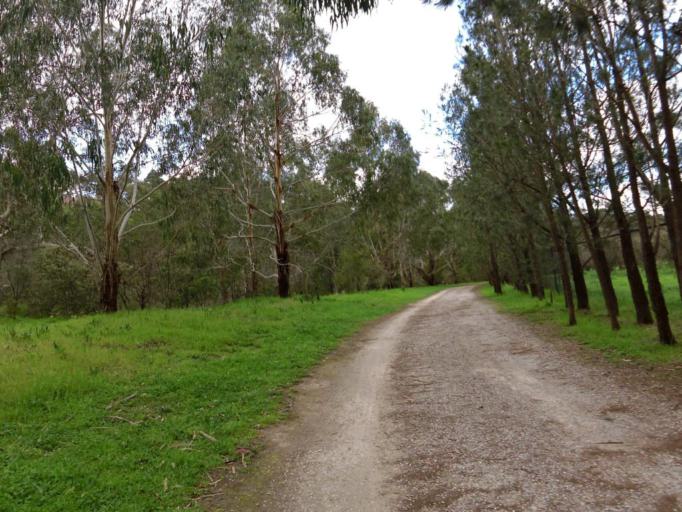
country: AU
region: Victoria
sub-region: Nillumbik
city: Eltham
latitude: -37.7352
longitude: 145.1532
